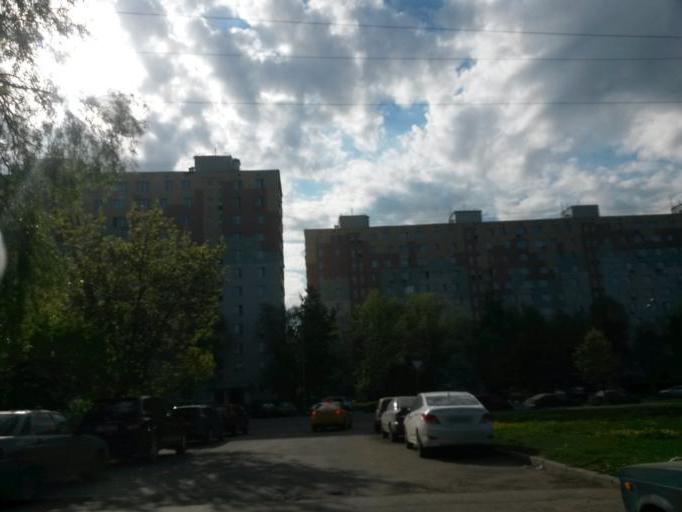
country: RU
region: Moscow
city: Mar'ino
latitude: 55.6544
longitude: 37.7107
